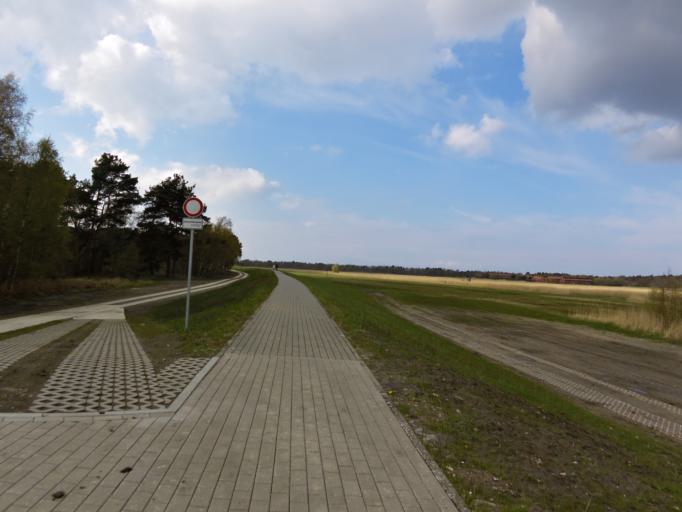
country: DE
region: Mecklenburg-Vorpommern
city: Zingst
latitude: 54.4327
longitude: 12.7174
